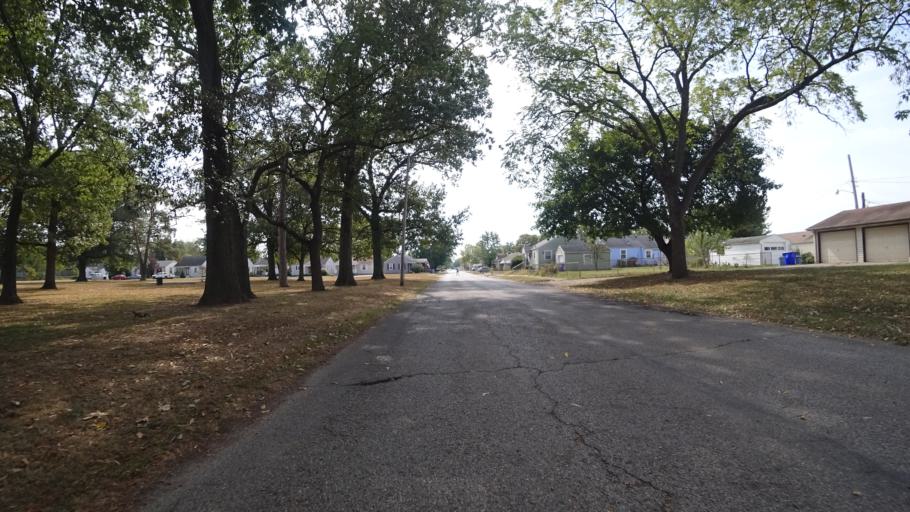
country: US
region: Ohio
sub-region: Butler County
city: Fairfield
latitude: 39.3608
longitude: -84.5531
